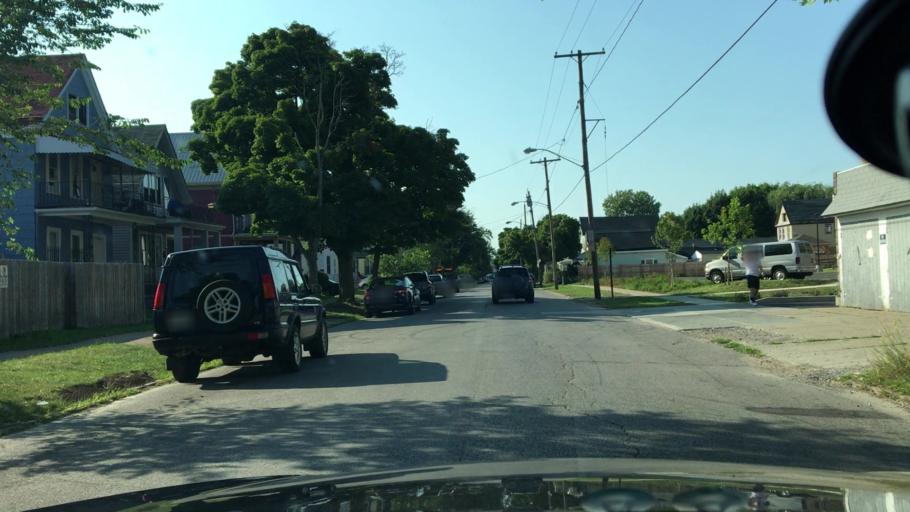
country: US
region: New York
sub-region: Erie County
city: Buffalo
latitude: 42.9085
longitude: -78.8921
